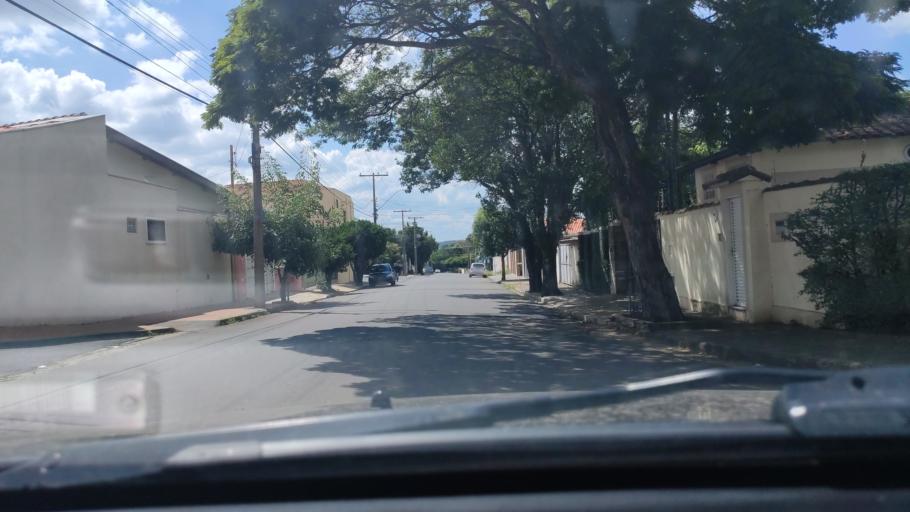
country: BR
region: Sao Paulo
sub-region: Sao Carlos
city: Sao Carlos
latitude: -21.9986
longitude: -47.8786
